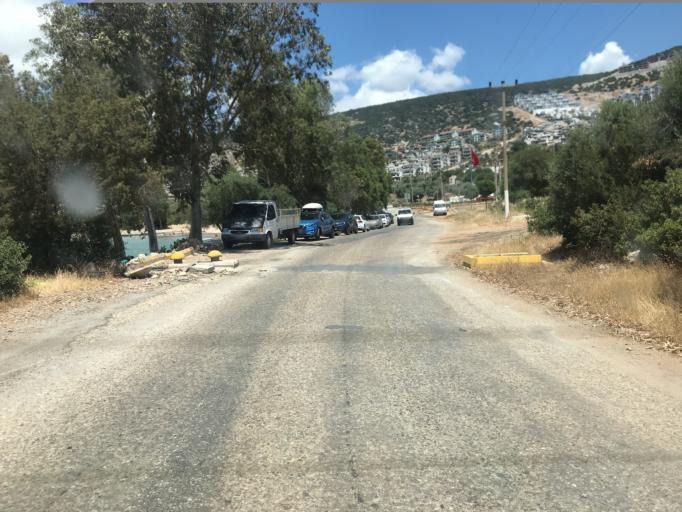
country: TR
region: Aydin
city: Sarikemer
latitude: 37.4124
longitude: 27.4225
